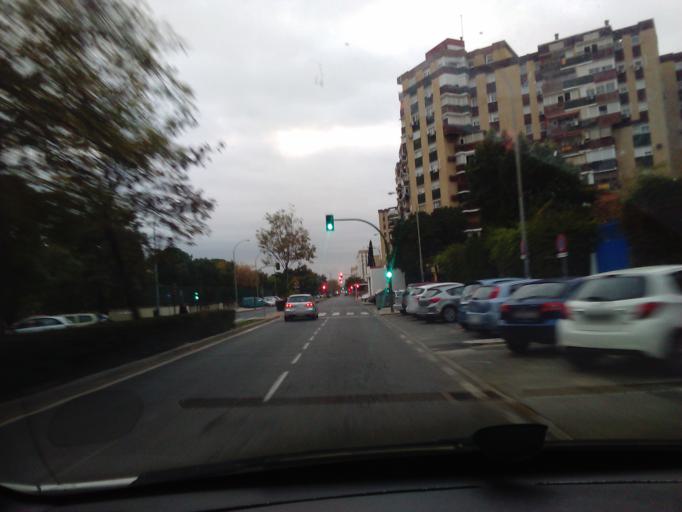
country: ES
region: Andalusia
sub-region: Provincia de Sevilla
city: Sevilla
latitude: 37.3847
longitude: -5.9447
